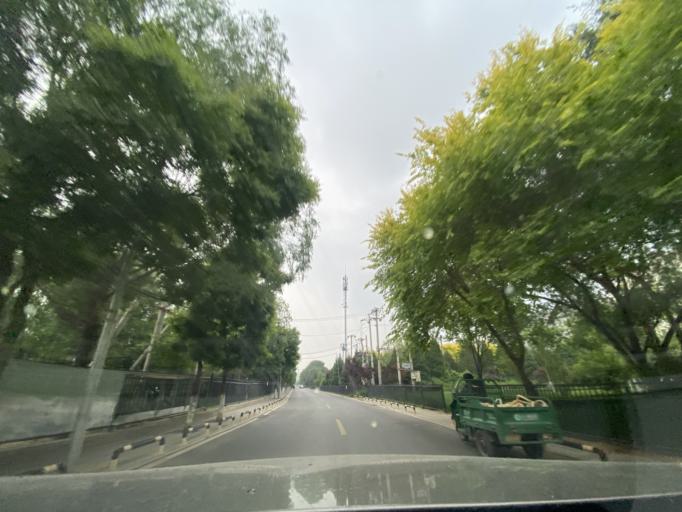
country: CN
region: Beijing
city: Sijiqing
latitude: 39.9546
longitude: 116.2483
